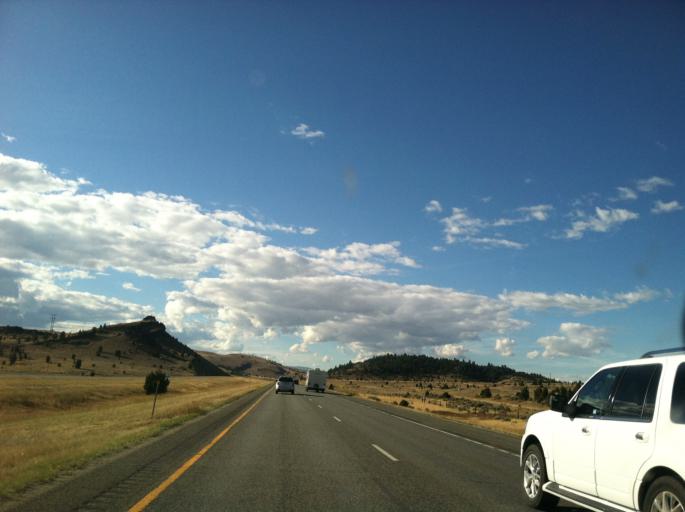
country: US
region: Montana
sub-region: Silver Bow County
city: Butte-Silver Bow (Balance)
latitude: 46.0152
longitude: -112.7154
